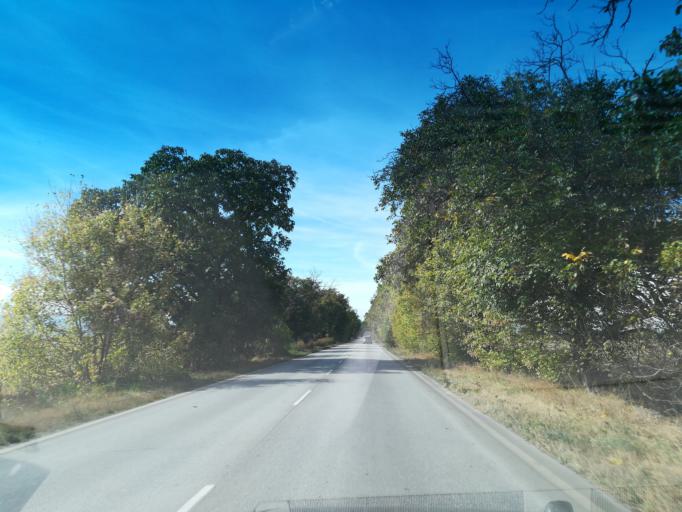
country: BG
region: Plovdiv
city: Stamboliyski
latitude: 42.1351
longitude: 24.6297
